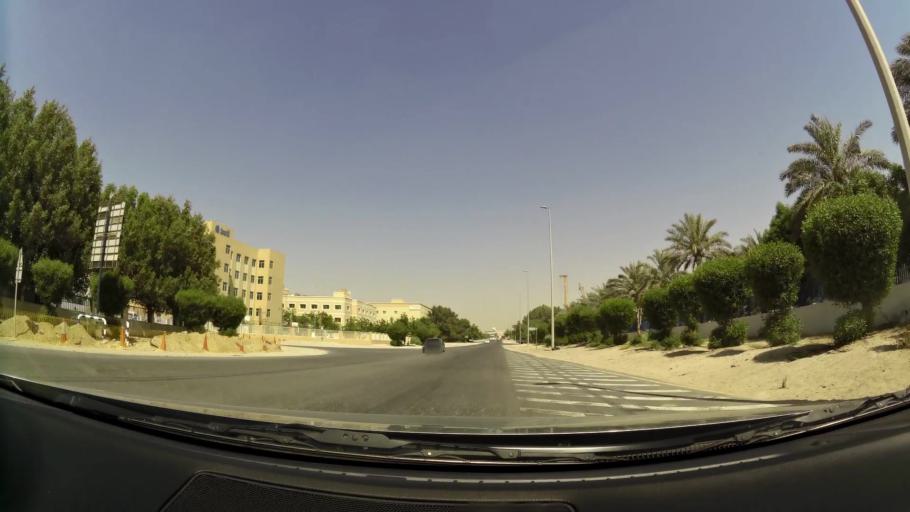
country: AE
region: Dubai
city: Dubai
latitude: 24.9726
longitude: 55.1646
